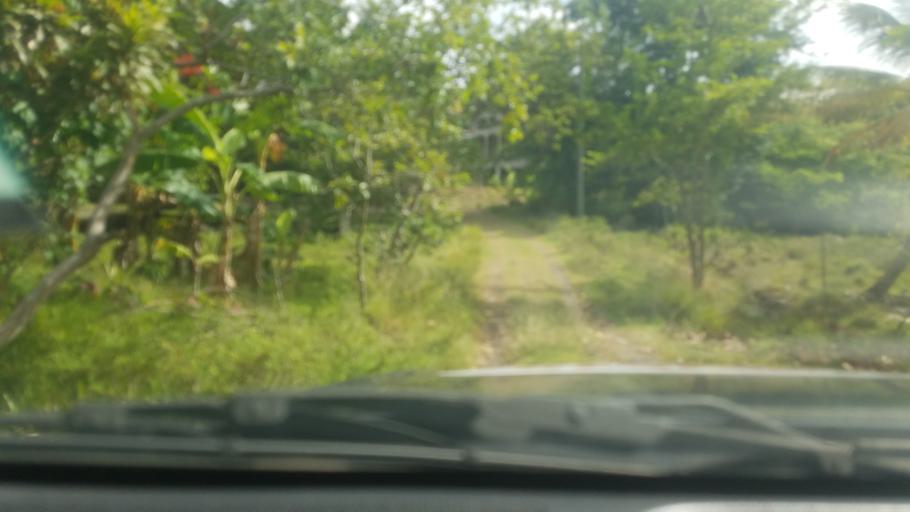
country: LC
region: Micoud Quarter
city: Micoud
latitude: 13.7946
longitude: -60.9145
